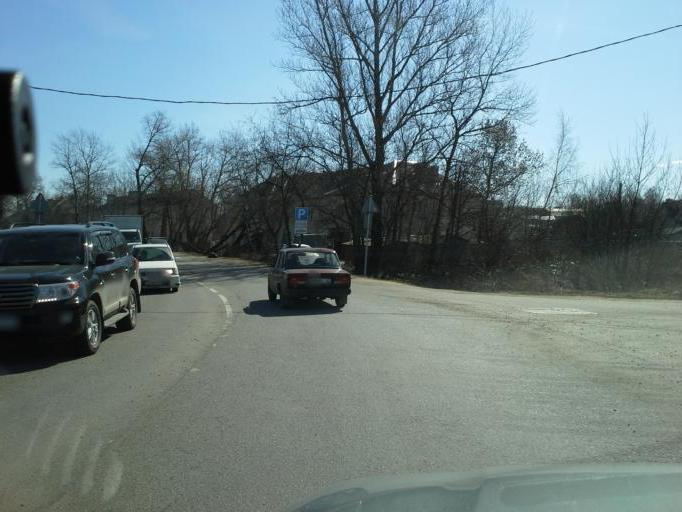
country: RU
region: Moskovskaya
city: Odintsovo
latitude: 55.6487
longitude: 37.2654
